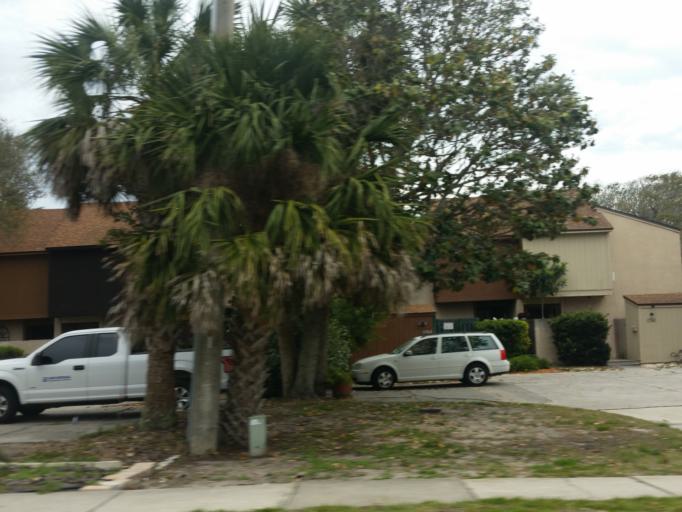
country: US
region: Florida
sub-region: Duval County
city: Atlantic Beach
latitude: 30.3445
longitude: -81.3994
